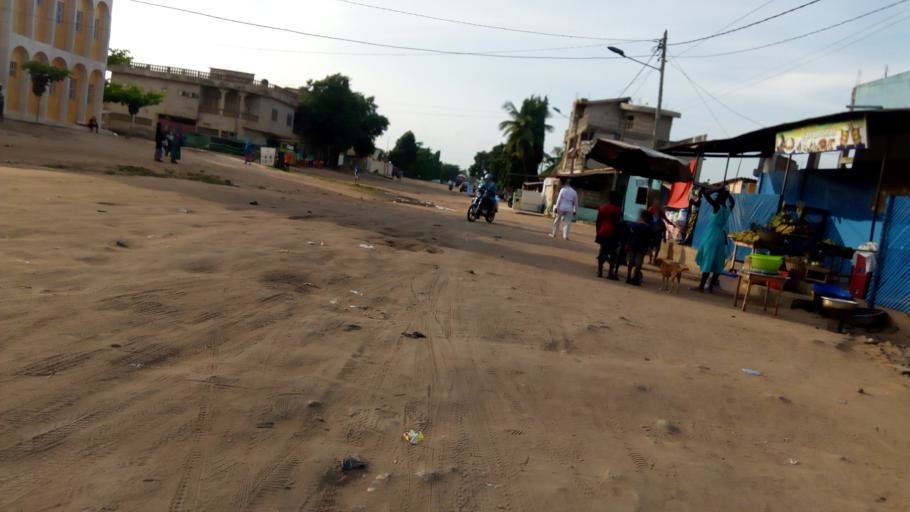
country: TG
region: Maritime
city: Lome
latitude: 6.1862
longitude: 1.1844
